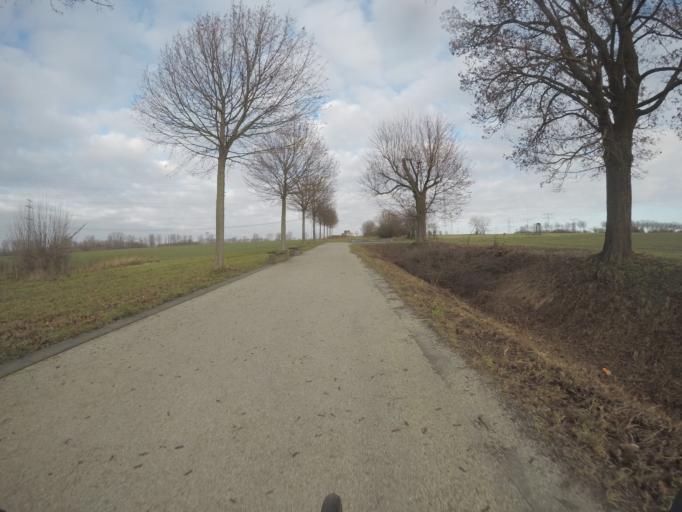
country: DE
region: Berlin
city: Wartenberg
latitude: 52.5906
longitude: 13.5049
